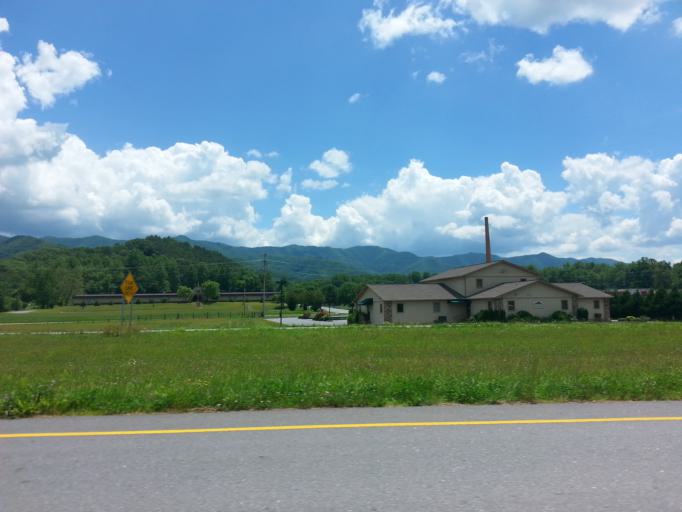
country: US
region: North Carolina
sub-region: Cherokee County
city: Andrews
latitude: 35.1975
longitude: -83.7975
